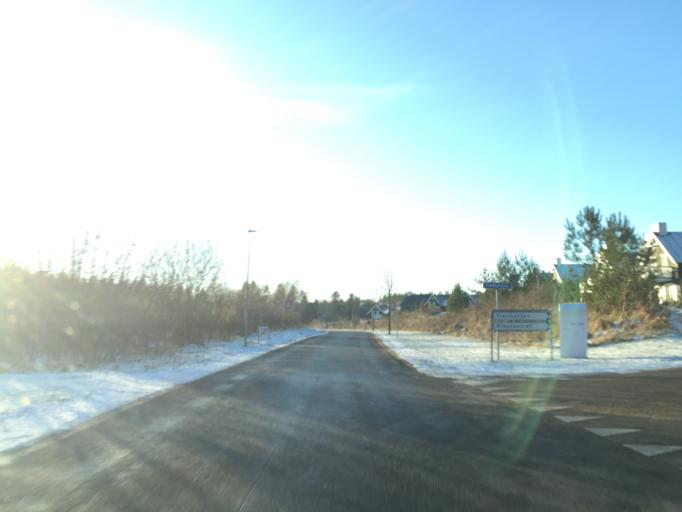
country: DK
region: Central Jutland
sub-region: Silkeborg Kommune
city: Svejbaek
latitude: 56.2166
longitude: 9.7274
